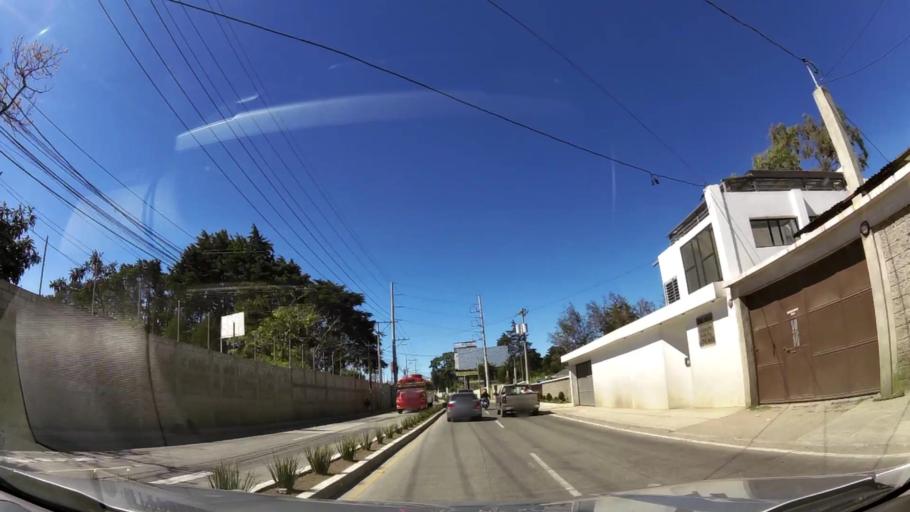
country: GT
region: Guatemala
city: San Jose Pinula
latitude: 14.5446
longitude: -90.4286
